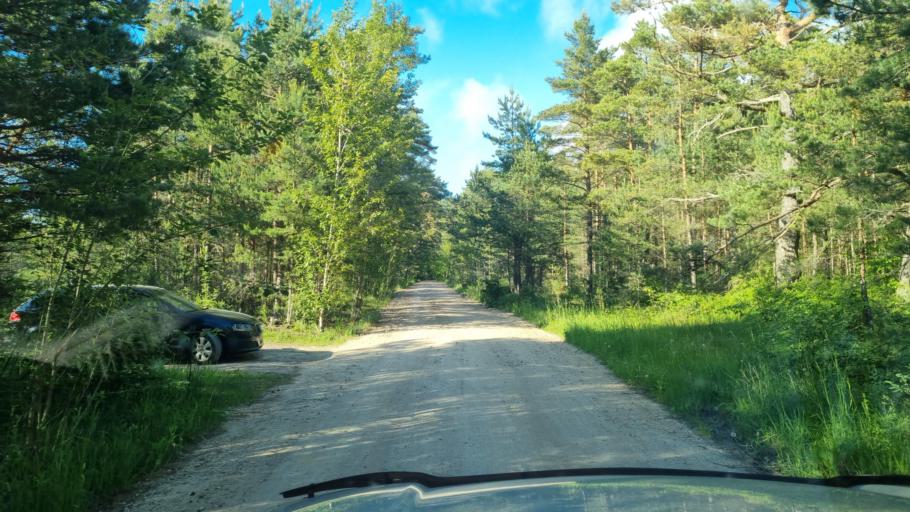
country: LV
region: Ventspils
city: Ventspils
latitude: 57.3661
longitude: 21.5148
